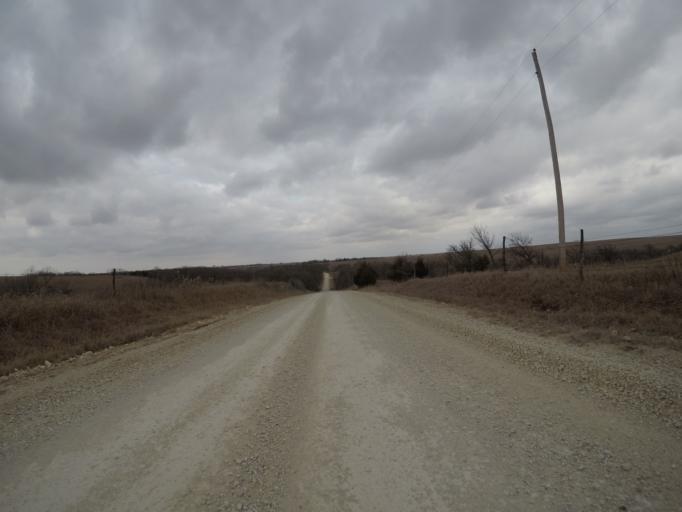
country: US
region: Kansas
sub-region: Morris County
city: Council Grove
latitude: 38.7593
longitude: -96.2794
